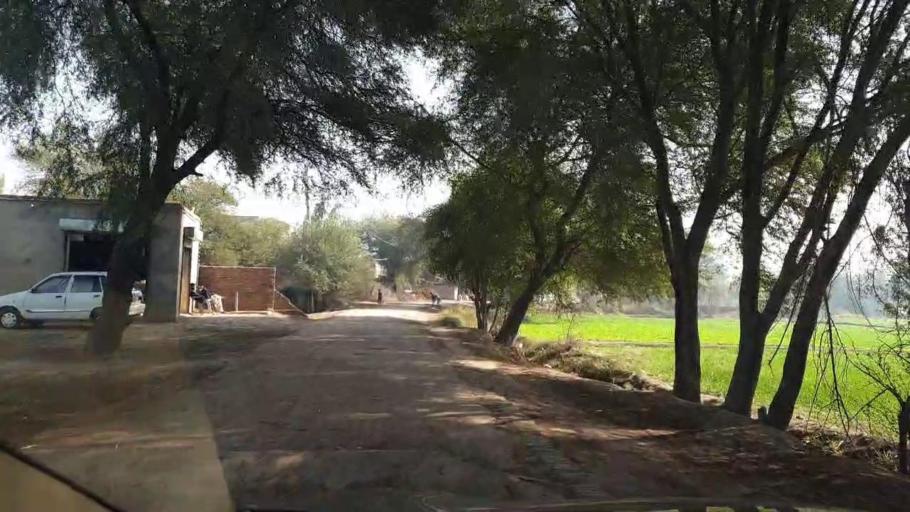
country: PK
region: Sindh
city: Ubauro
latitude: 28.1140
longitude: 69.7284
